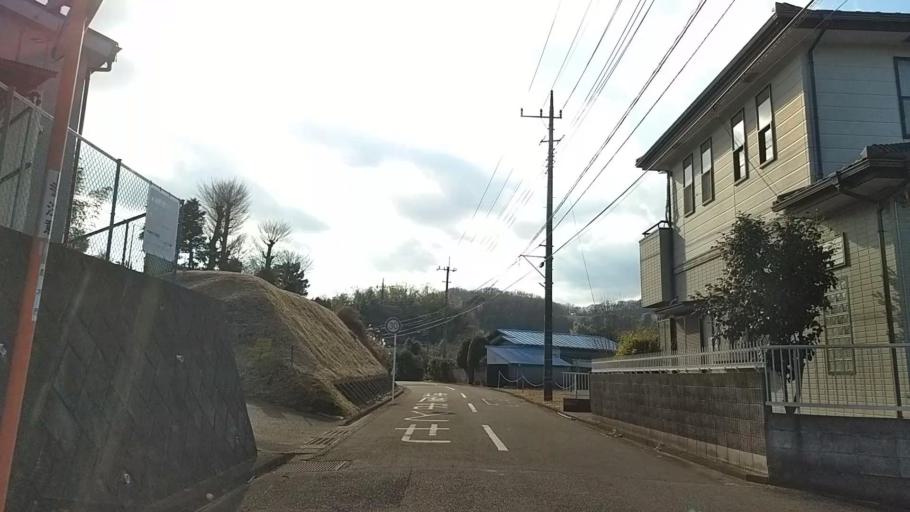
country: JP
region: Kanagawa
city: Isehara
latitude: 35.4303
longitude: 139.3177
